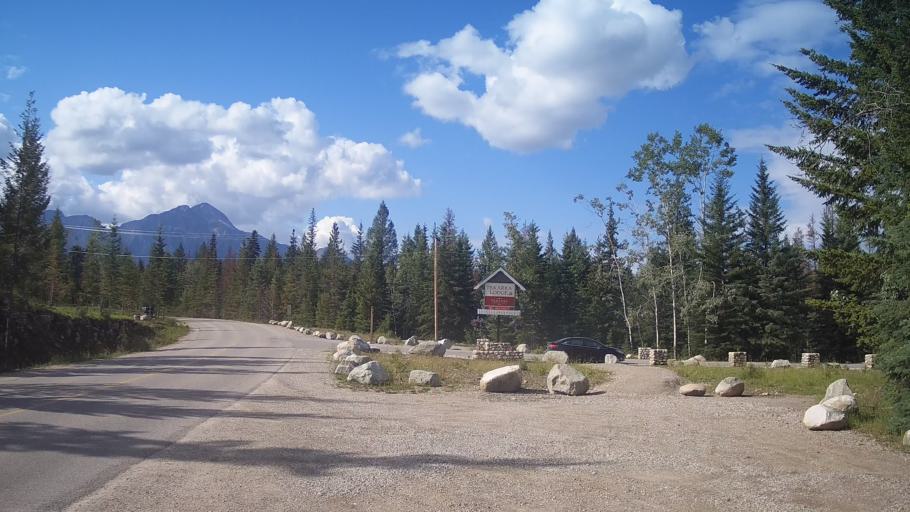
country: CA
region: Alberta
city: Jasper Park Lodge
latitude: 52.8662
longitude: -118.0708
